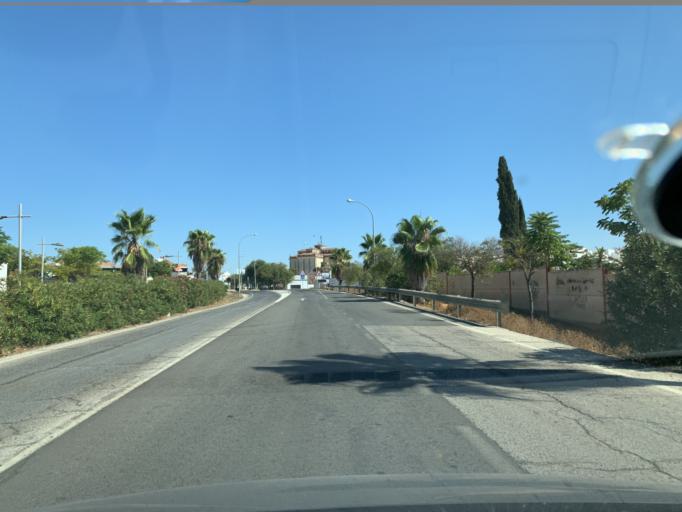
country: ES
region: Andalusia
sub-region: Provincia de Sevilla
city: Carmona
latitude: 37.4663
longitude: -5.6517
